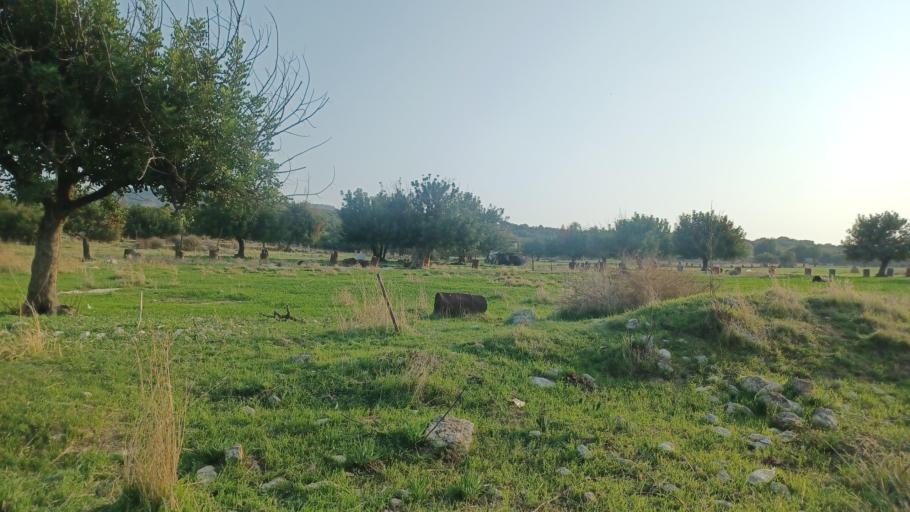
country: CY
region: Pafos
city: Polis
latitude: 34.9647
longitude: 32.4847
